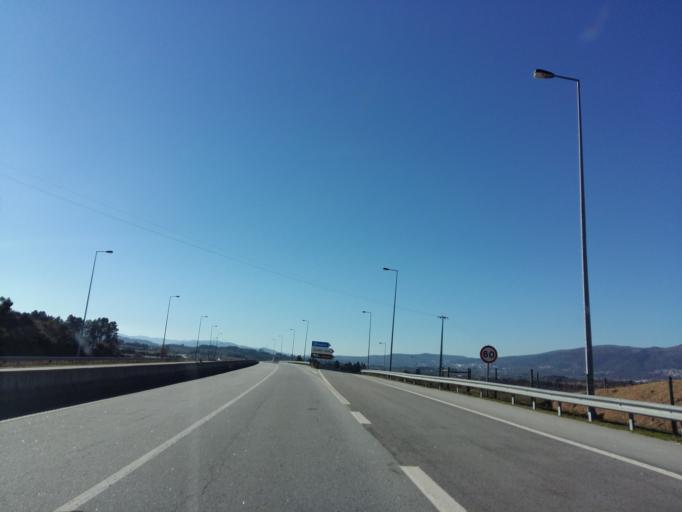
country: PT
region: Castelo Branco
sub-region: Covilha
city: Teixoso
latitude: 40.2644
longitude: -7.4367
